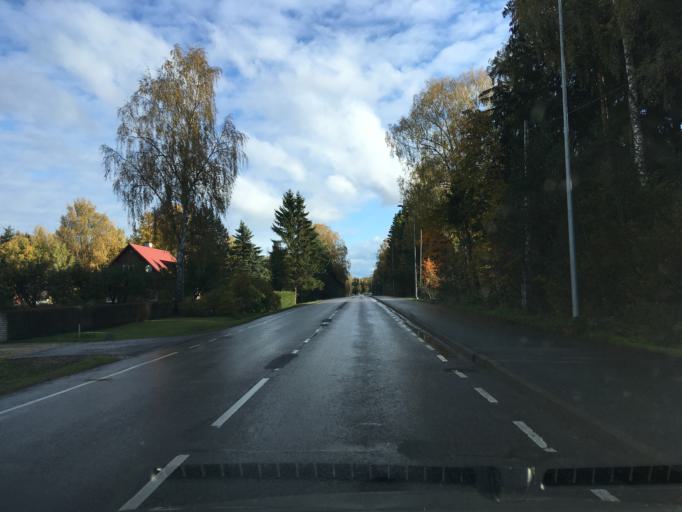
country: EE
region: Harju
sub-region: Raasiku vald
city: Raasiku
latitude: 59.1882
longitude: 25.1745
